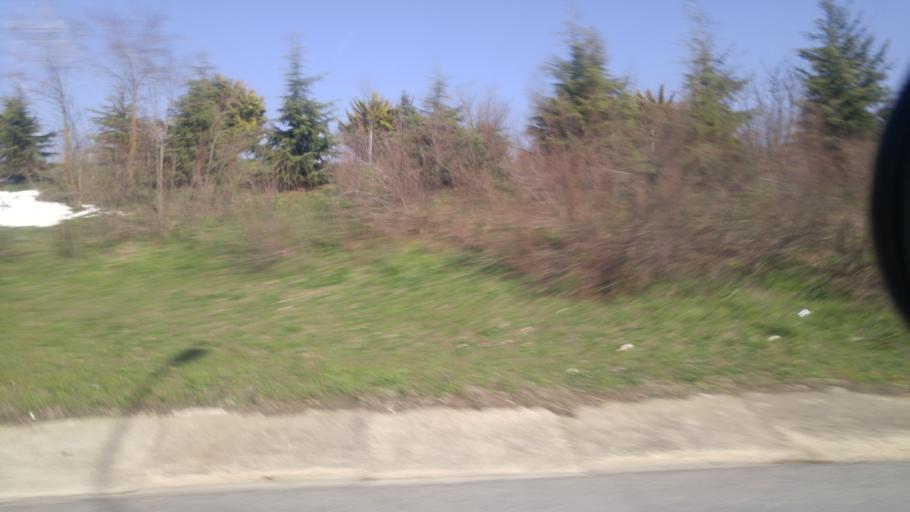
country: TR
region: Istanbul
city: Celaliye
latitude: 41.0610
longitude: 28.4097
